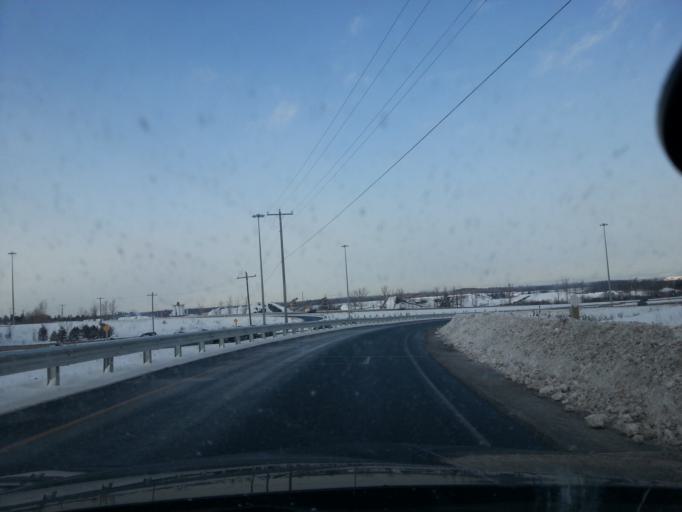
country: CA
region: Ontario
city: Bells Corners
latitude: 45.2803
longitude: -75.9555
